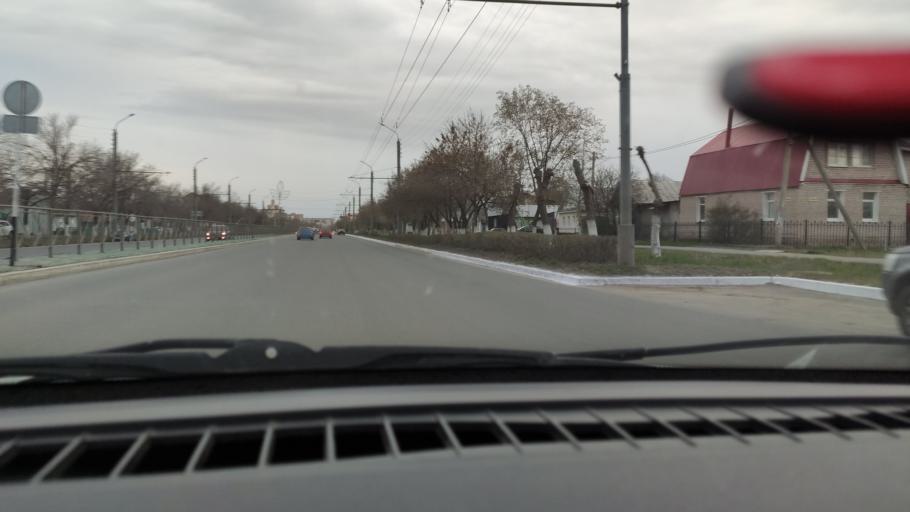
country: RU
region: Orenburg
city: Orenburg
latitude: 51.7918
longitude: 55.1067
